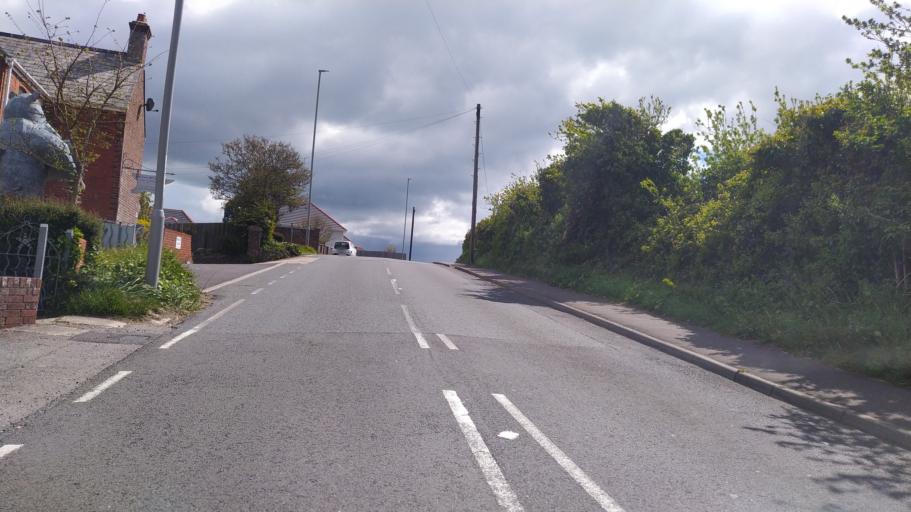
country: GB
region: England
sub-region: Dorset
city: Chickerell
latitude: 50.6240
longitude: -2.5092
